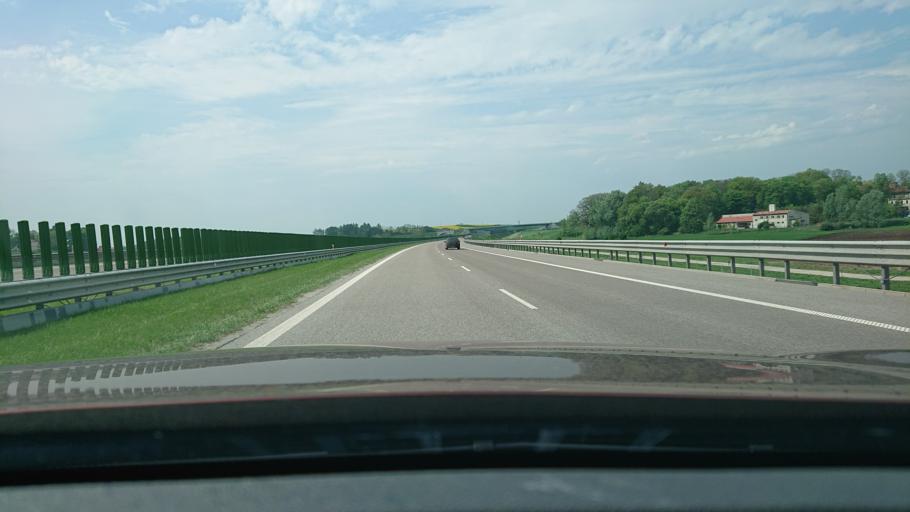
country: PL
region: Subcarpathian Voivodeship
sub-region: Powiat jaroslawski
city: Rokietnica
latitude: 49.9395
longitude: 22.6764
